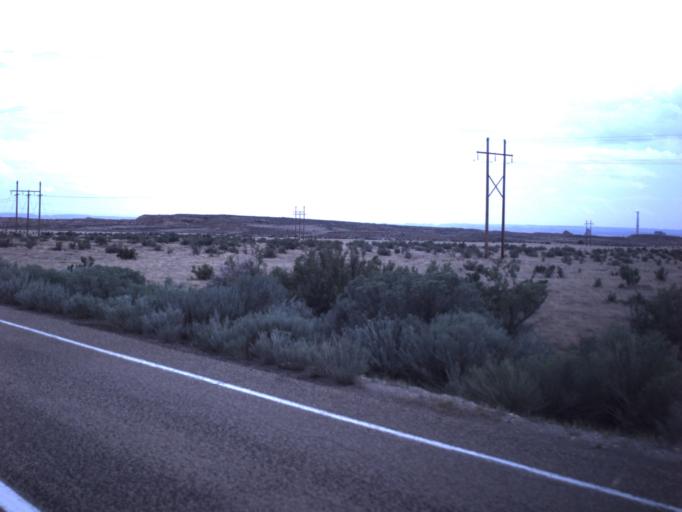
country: US
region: Utah
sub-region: Uintah County
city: Naples
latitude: 40.1343
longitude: -109.2669
